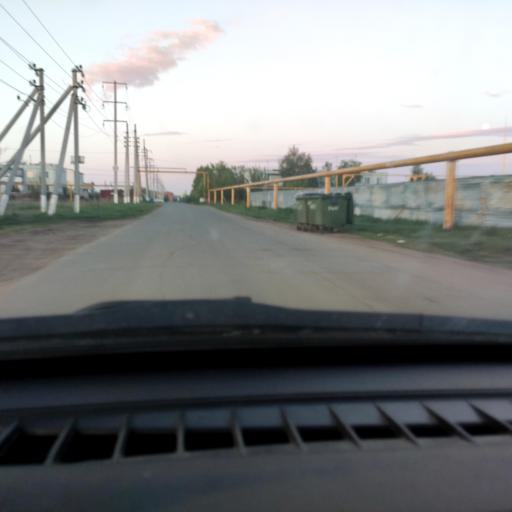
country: RU
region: Samara
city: Podstepki
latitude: 53.5205
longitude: 49.1130
